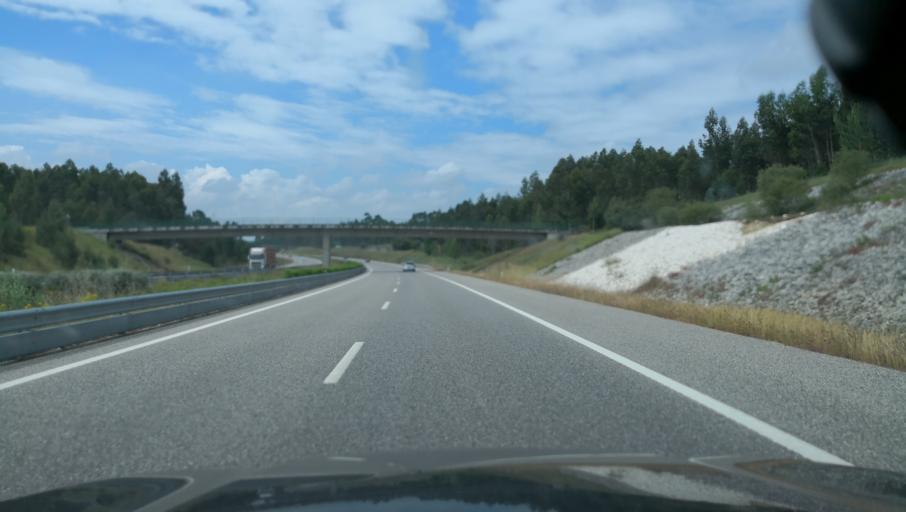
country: PT
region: Leiria
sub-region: Leiria
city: Amor
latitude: 39.7844
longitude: -8.8669
